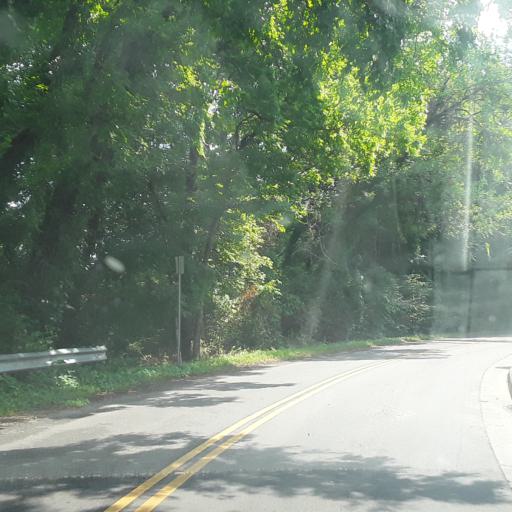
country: US
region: Tennessee
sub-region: Davidson County
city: Oak Hill
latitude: 36.1159
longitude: -86.7343
